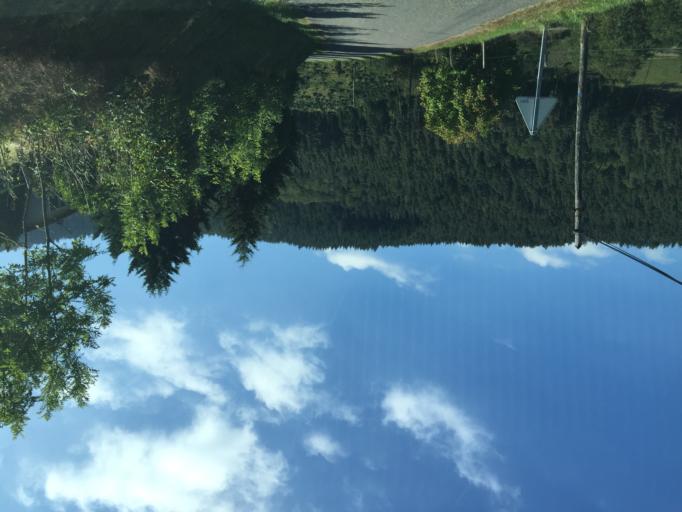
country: FR
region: Rhone-Alpes
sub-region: Departement de la Loire
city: Saint-Paul-en-Jarez
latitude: 45.4203
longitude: 4.5608
